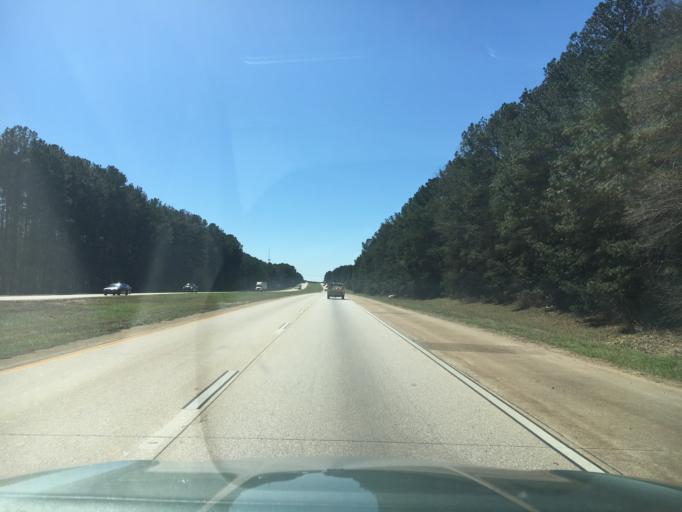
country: US
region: Georgia
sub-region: Troup County
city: La Grange
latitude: 33.0312
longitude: -84.9784
